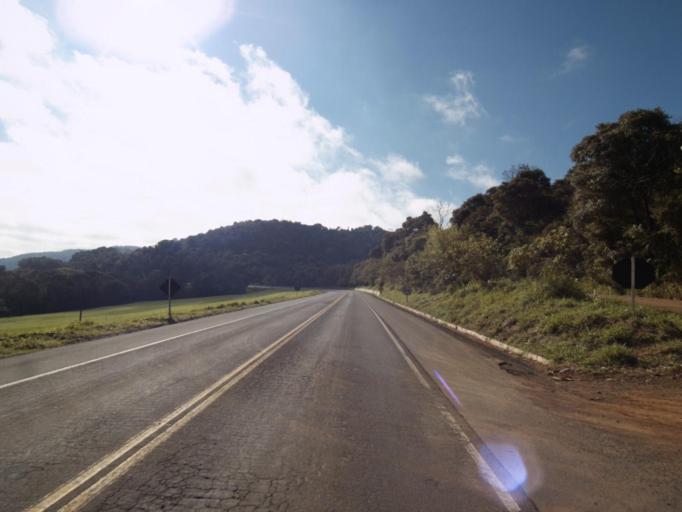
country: BR
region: Rio Grande do Sul
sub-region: Frederico Westphalen
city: Frederico Westphalen
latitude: -27.1583
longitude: -53.2188
